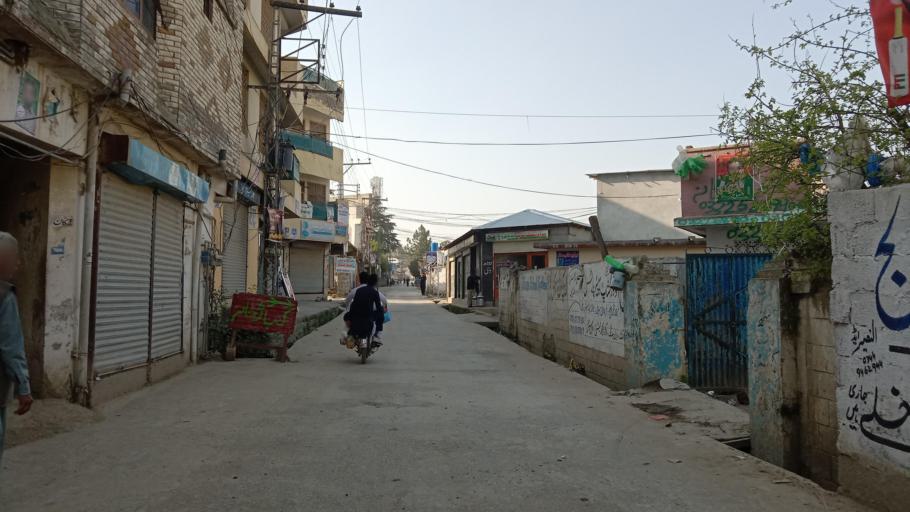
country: PK
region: Khyber Pakhtunkhwa
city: Abbottabad
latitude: 34.1984
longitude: 73.2286
